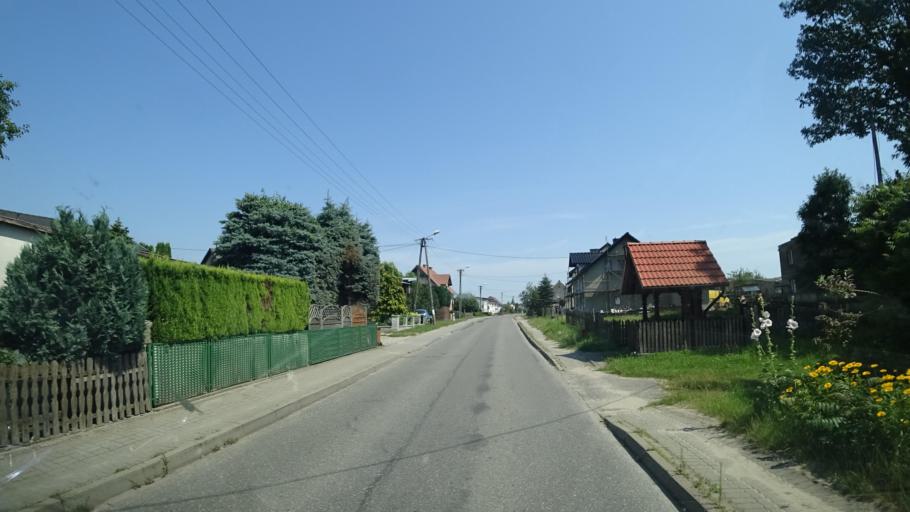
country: PL
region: Pomeranian Voivodeship
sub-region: Powiat chojnicki
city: Brusy
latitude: 53.8729
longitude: 17.6796
